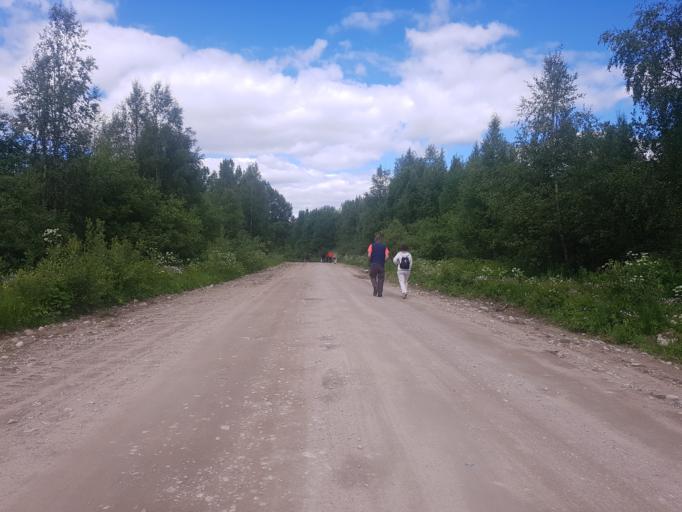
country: RU
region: Republic of Karelia
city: Kostomuksha
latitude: 65.1846
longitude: 30.2908
